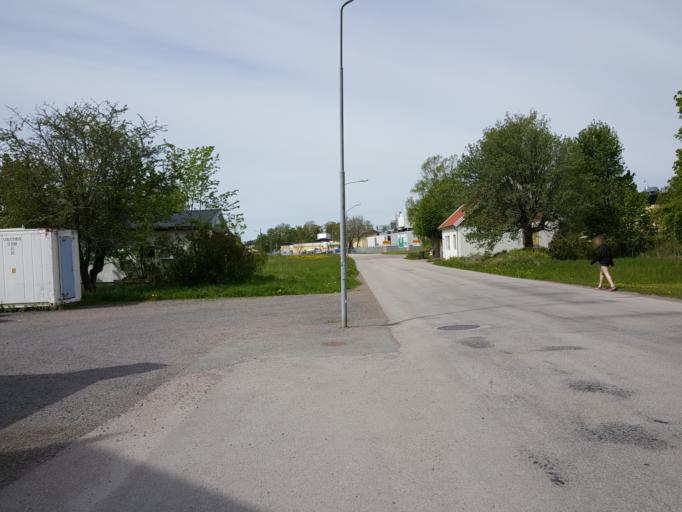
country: SE
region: Uppsala
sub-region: Osthammars Kommun
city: Gimo
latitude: 60.1762
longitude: 18.1873
